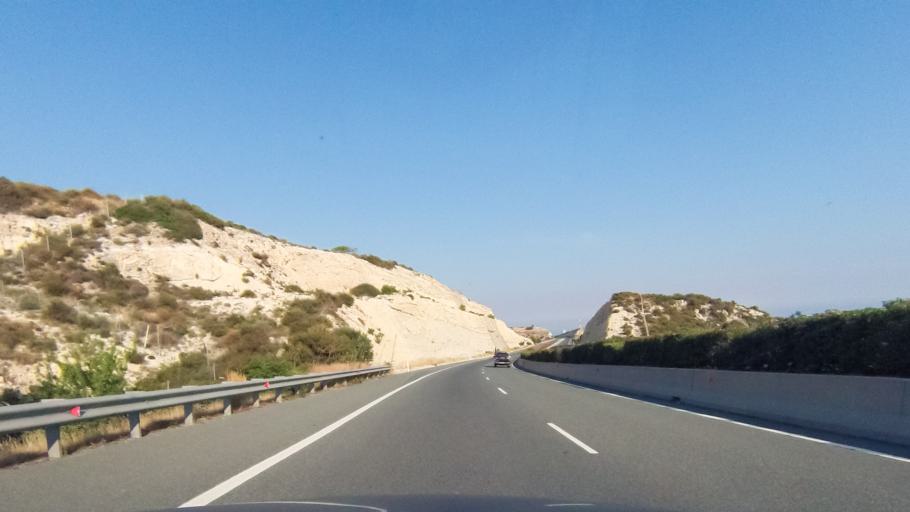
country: CY
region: Limassol
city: Sotira
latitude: 34.6918
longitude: 32.8685
